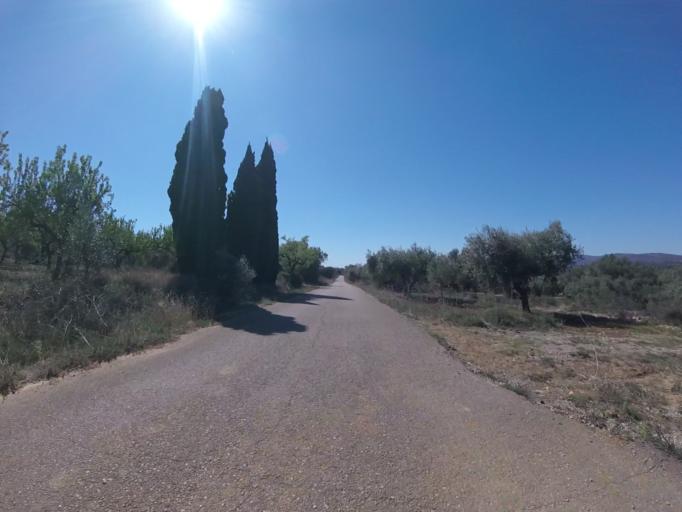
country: ES
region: Valencia
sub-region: Provincia de Castello
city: Cuevas de Vinroma
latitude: 40.3857
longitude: 0.1578
